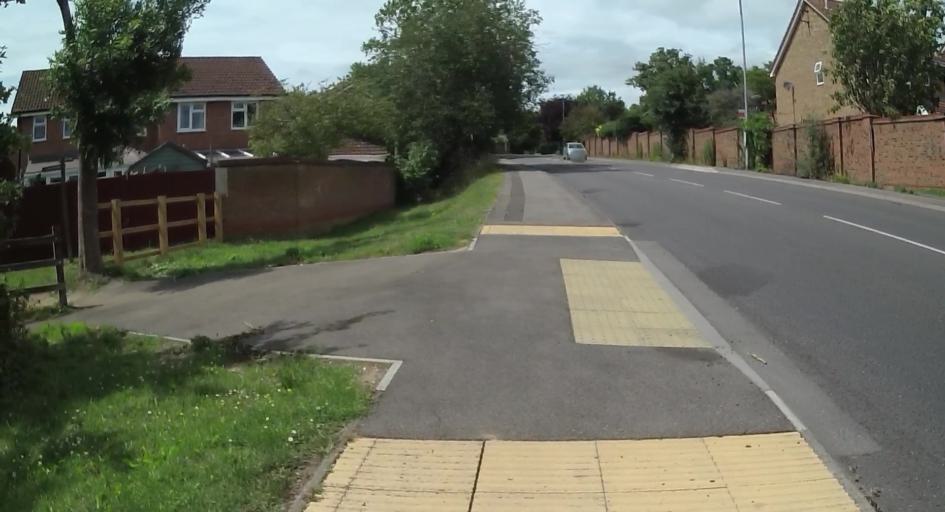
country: GB
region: England
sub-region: Wokingham
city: Lower Earley
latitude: 51.4211
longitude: -0.9336
